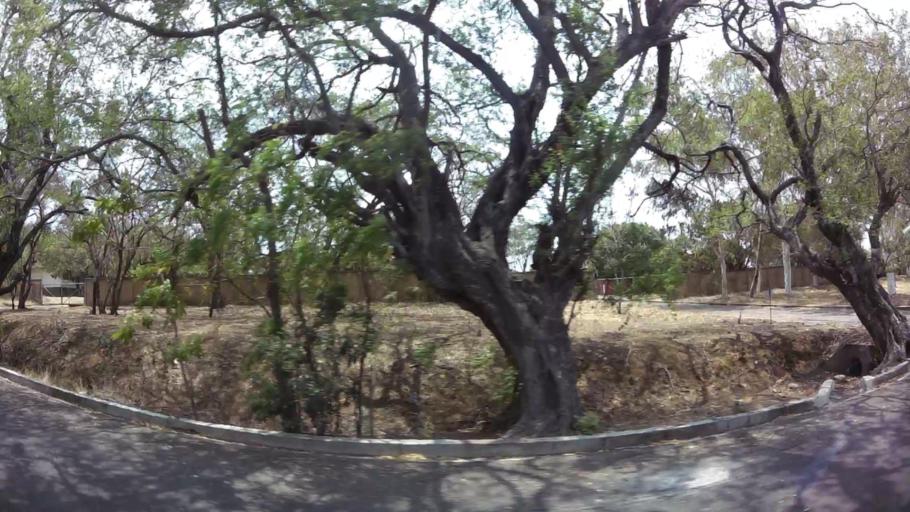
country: NI
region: Managua
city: Managua
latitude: 12.1189
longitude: -86.2864
